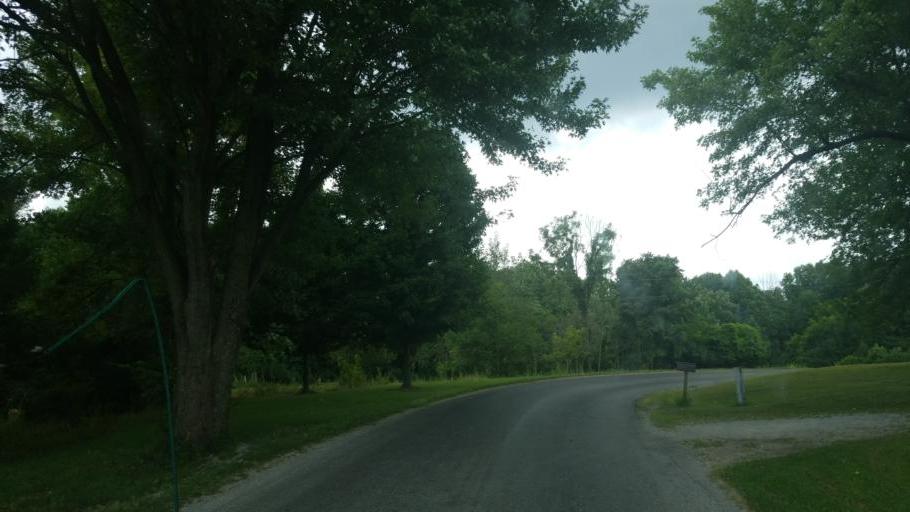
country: US
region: Illinois
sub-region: Jackson County
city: Murphysboro
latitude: 37.7039
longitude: -89.3321
